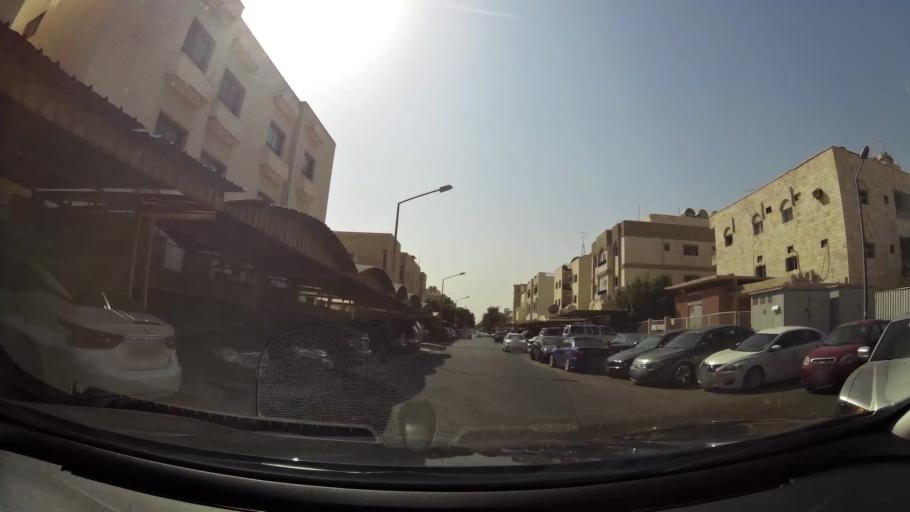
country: KW
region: Muhafazat Hawalli
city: Salwa
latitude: 29.2867
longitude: 48.0847
